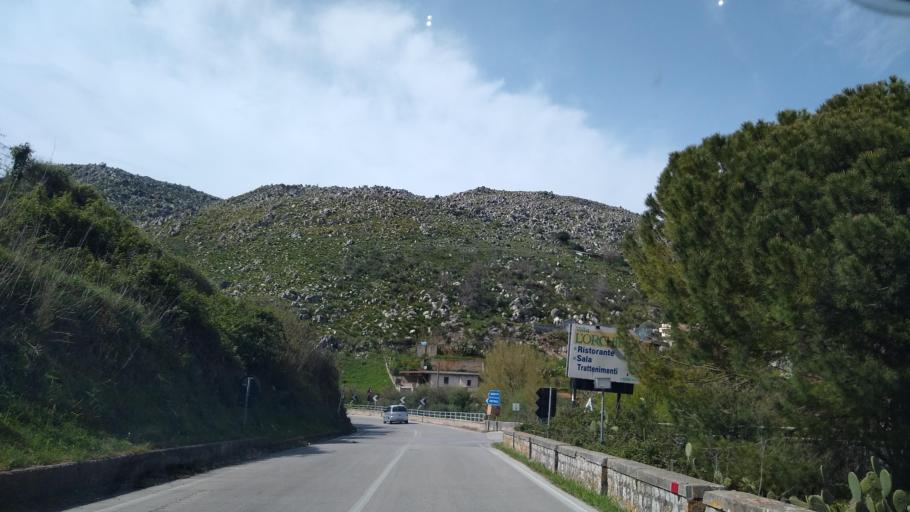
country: IT
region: Sicily
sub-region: Palermo
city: Pioppo
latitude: 38.0479
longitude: 13.1980
